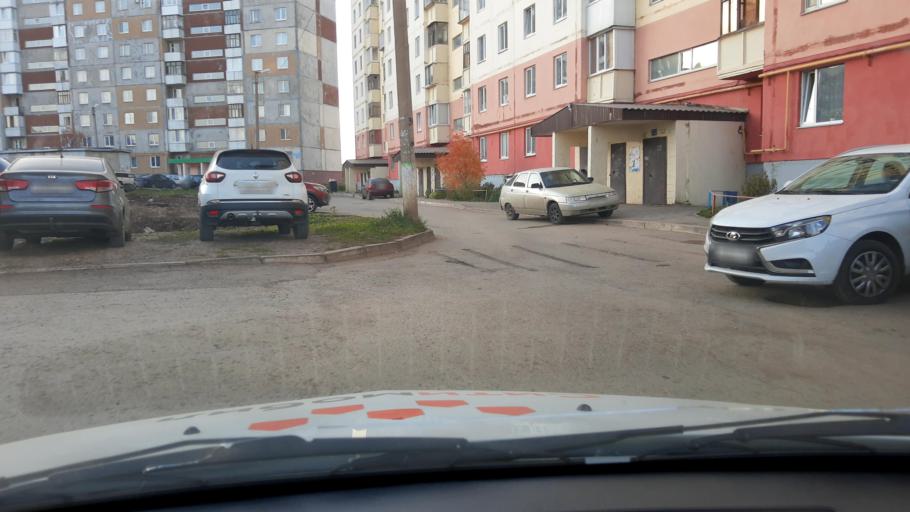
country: RU
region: Bashkortostan
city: Iglino
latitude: 54.7554
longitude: 56.2408
